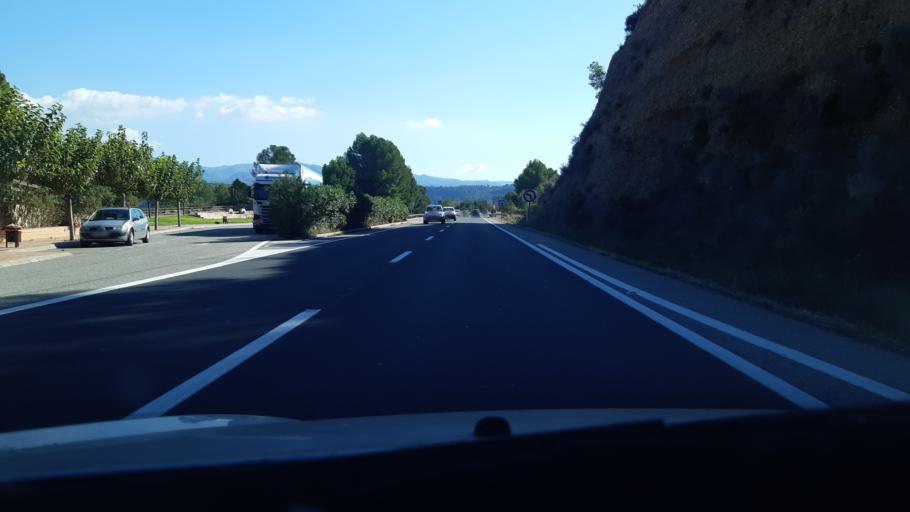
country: ES
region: Catalonia
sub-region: Provincia de Tarragona
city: Tivenys
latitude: 40.9208
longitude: 0.4915
